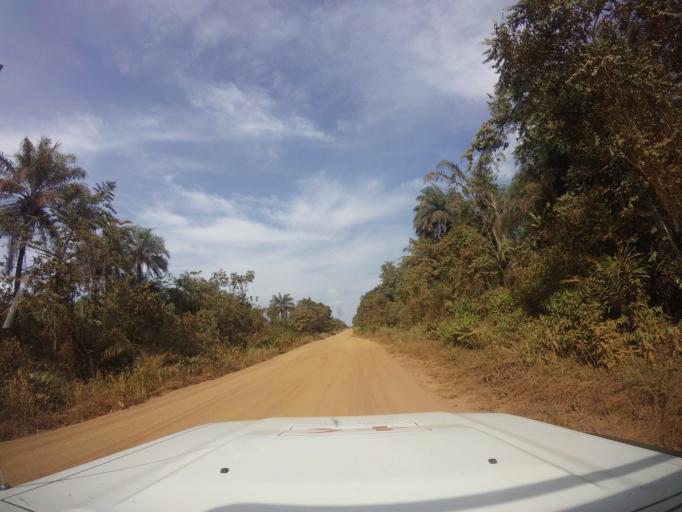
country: LR
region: Grand Cape Mount
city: Robertsport
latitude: 6.6810
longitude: -11.1333
